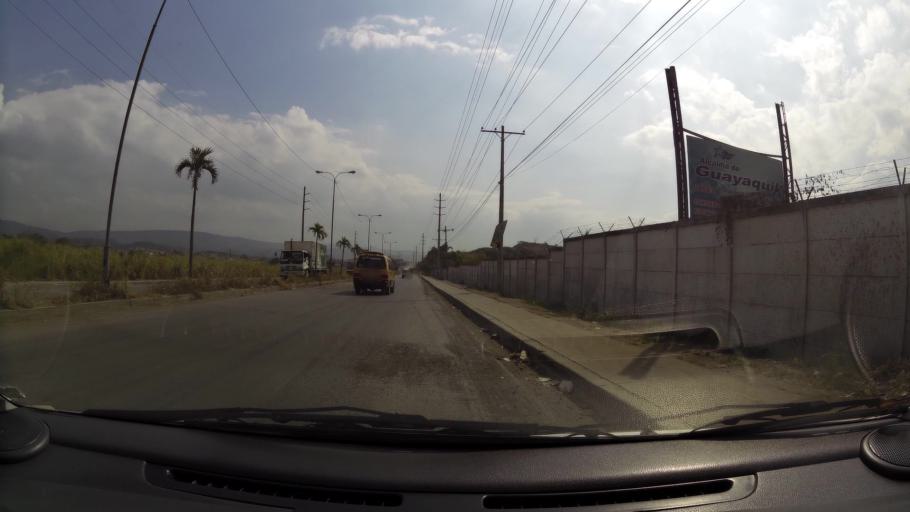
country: EC
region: Guayas
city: Santa Lucia
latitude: -2.1208
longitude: -79.9787
